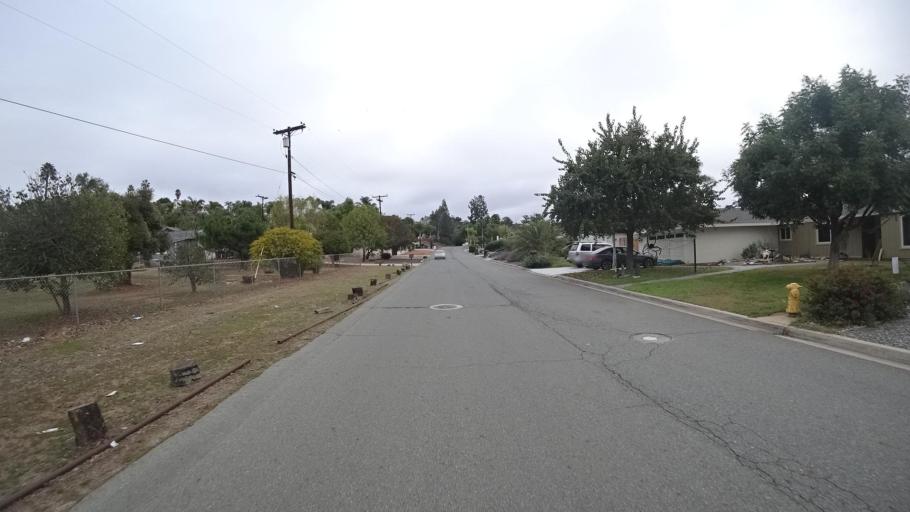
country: US
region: California
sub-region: San Diego County
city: Rancho San Diego
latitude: 32.7703
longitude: -116.9260
